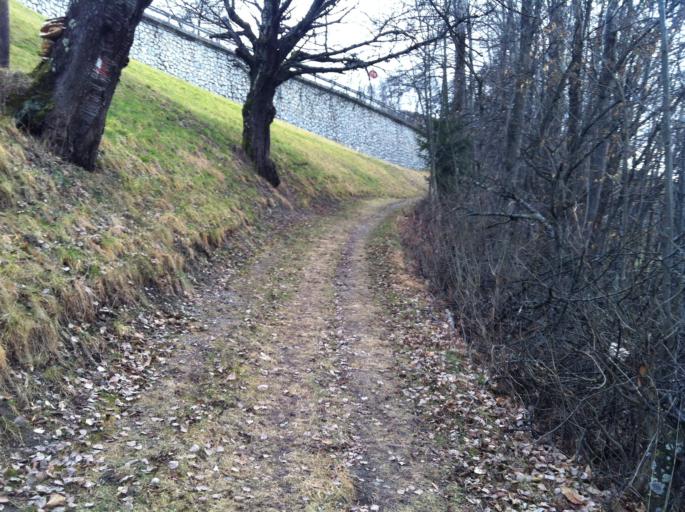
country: IT
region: Trentino-Alto Adige
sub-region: Bolzano
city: Bressanone
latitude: 46.6921
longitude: 11.6623
